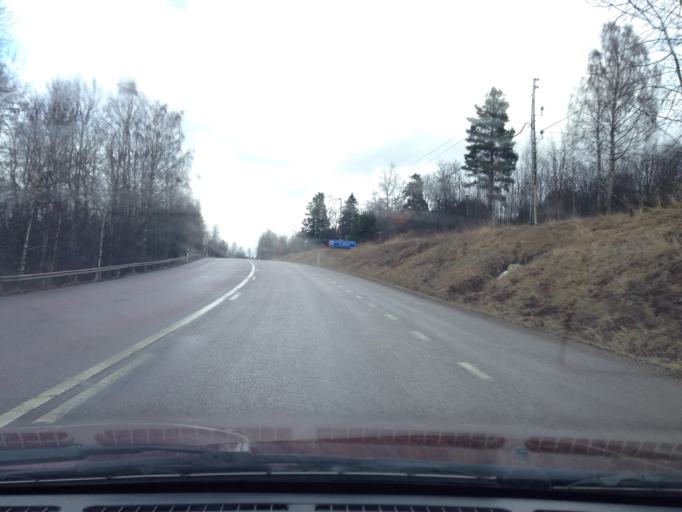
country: SE
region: Dalarna
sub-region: Ludvika Kommun
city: Ludvika
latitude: 60.1505
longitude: 15.2237
